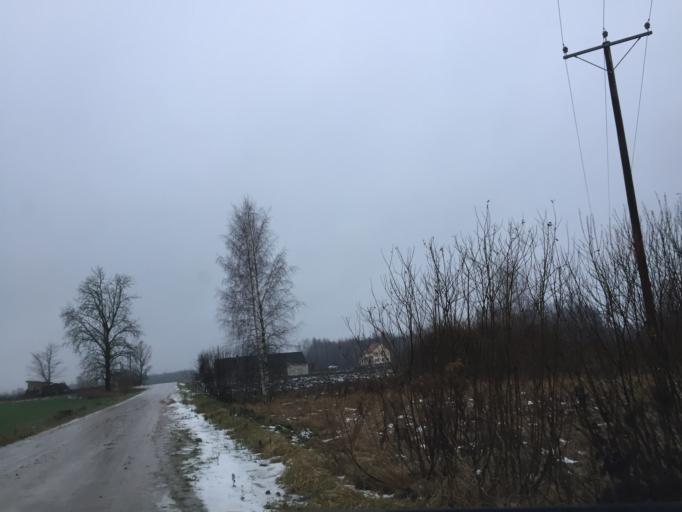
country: LV
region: Livani
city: Livani
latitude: 56.5334
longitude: 26.2445
